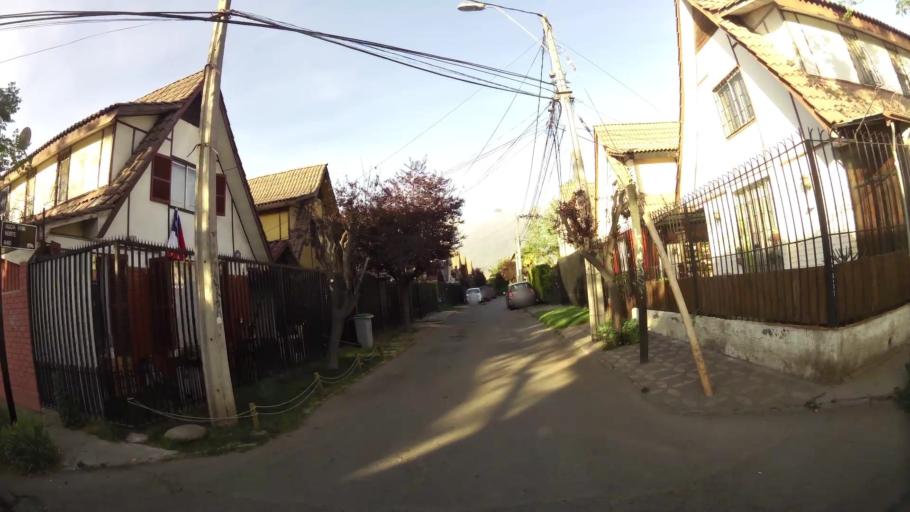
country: CL
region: Santiago Metropolitan
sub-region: Provincia de Cordillera
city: Puente Alto
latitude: -33.5468
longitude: -70.5778
